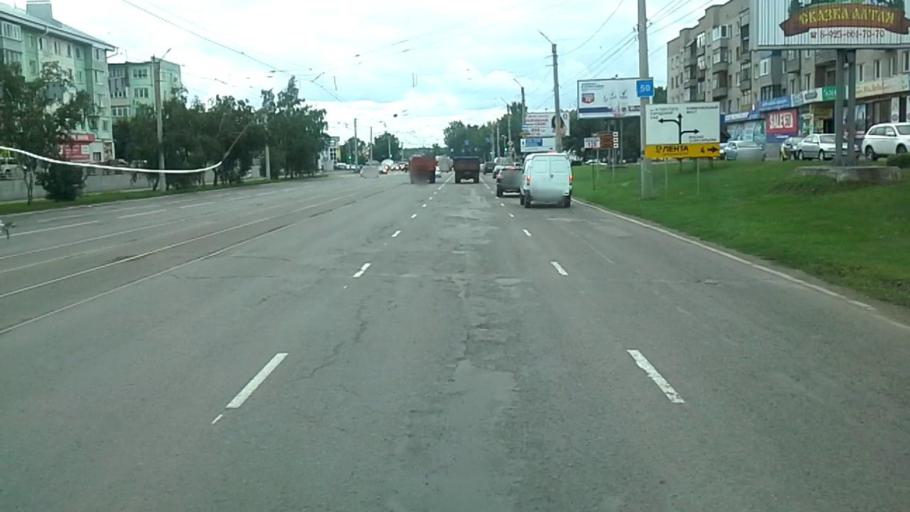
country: RU
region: Altai Krai
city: Biysk
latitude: 52.5429
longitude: 85.2181
